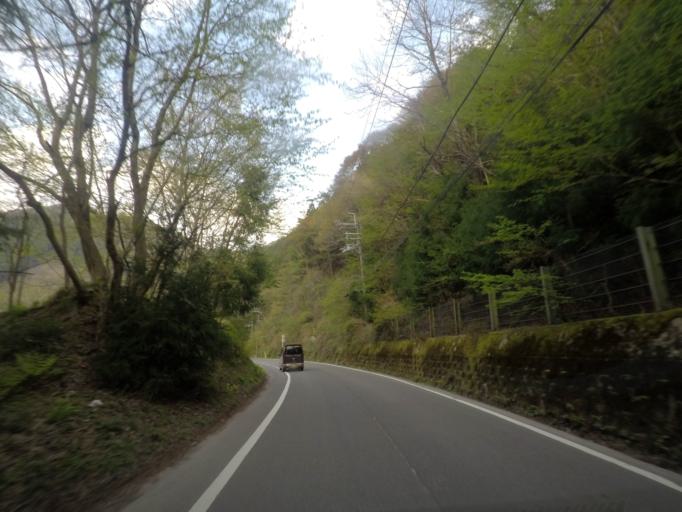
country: JP
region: Shiga Prefecture
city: Hino
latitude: 35.0840
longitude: 136.3545
